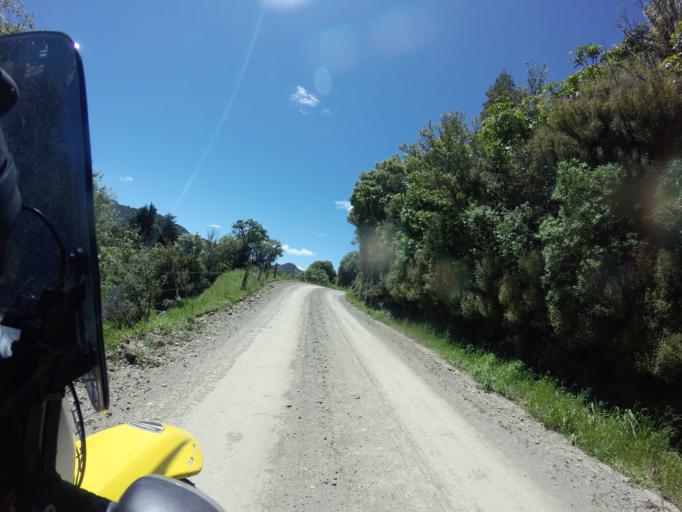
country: NZ
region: Bay of Plenty
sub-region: Opotiki District
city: Opotiki
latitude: -38.4028
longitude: 177.4555
